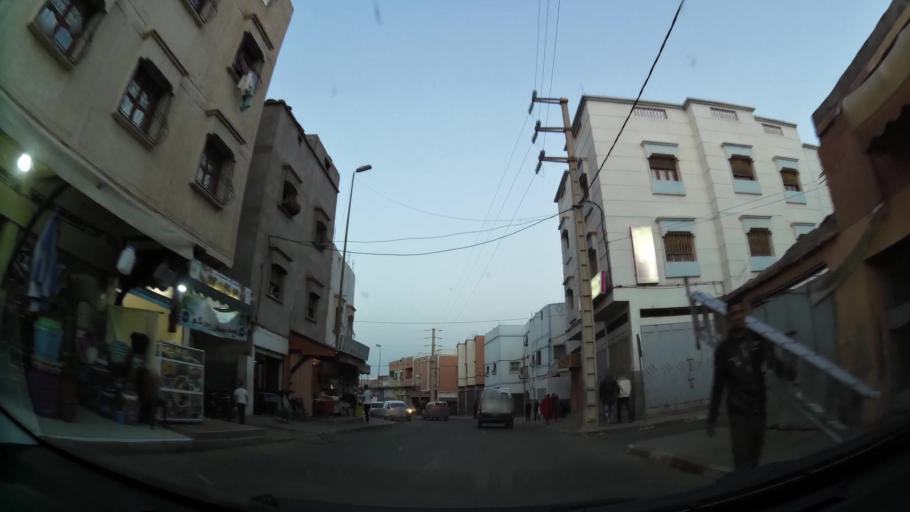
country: MA
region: Souss-Massa-Draa
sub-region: Inezgane-Ait Mellou
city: Inezgane
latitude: 30.3749
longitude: -9.4926
